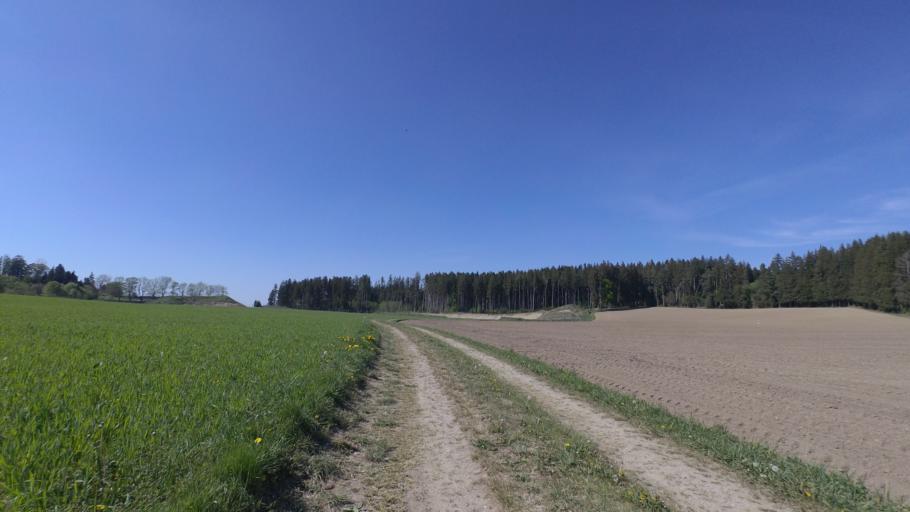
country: DE
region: Bavaria
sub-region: Upper Bavaria
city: Traunreut
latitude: 47.9418
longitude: 12.5580
